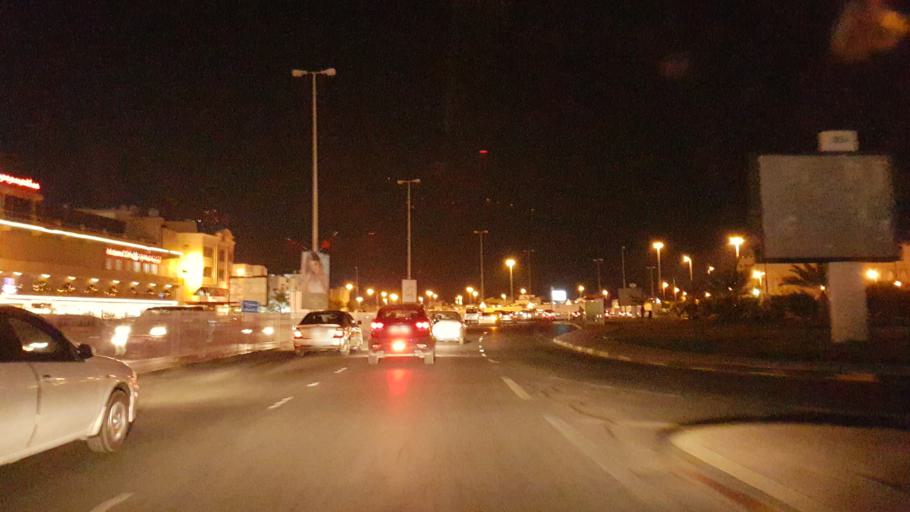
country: BH
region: Manama
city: Jidd Hafs
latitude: 26.2278
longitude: 50.5374
